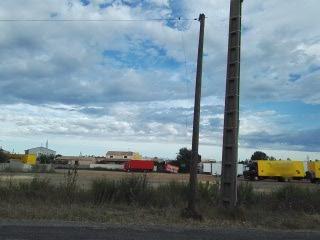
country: FR
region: Languedoc-Roussillon
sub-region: Departement de l'Herault
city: Marseillan
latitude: 43.3161
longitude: 3.5363
